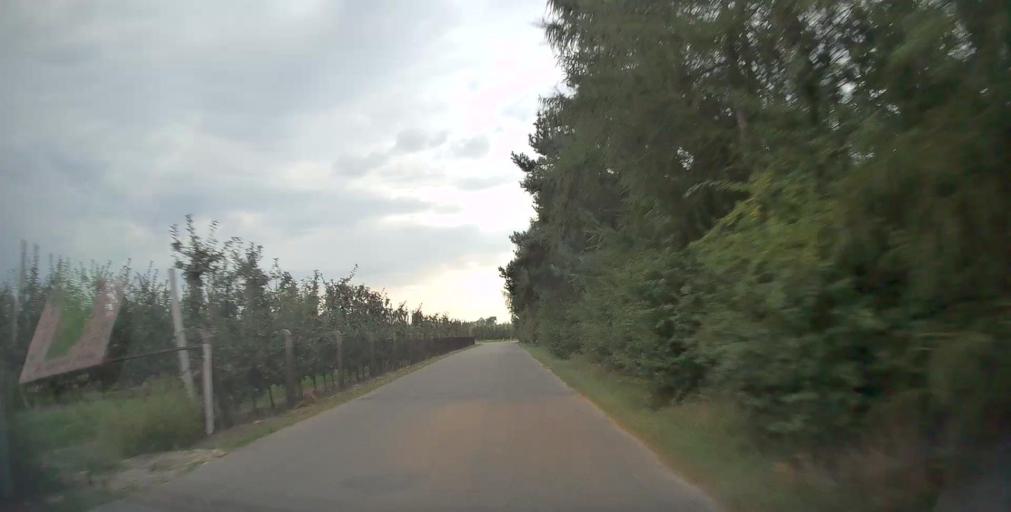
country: PL
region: Masovian Voivodeship
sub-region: Powiat grojecki
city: Jasieniec
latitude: 51.7944
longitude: 20.8950
